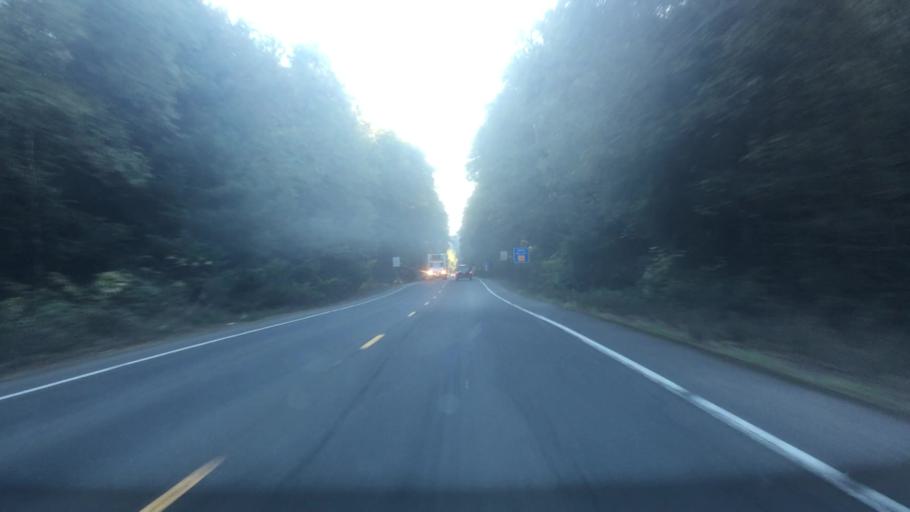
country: US
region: Oregon
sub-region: Clatsop County
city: Cannon Beach
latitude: 45.8939
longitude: -123.9559
